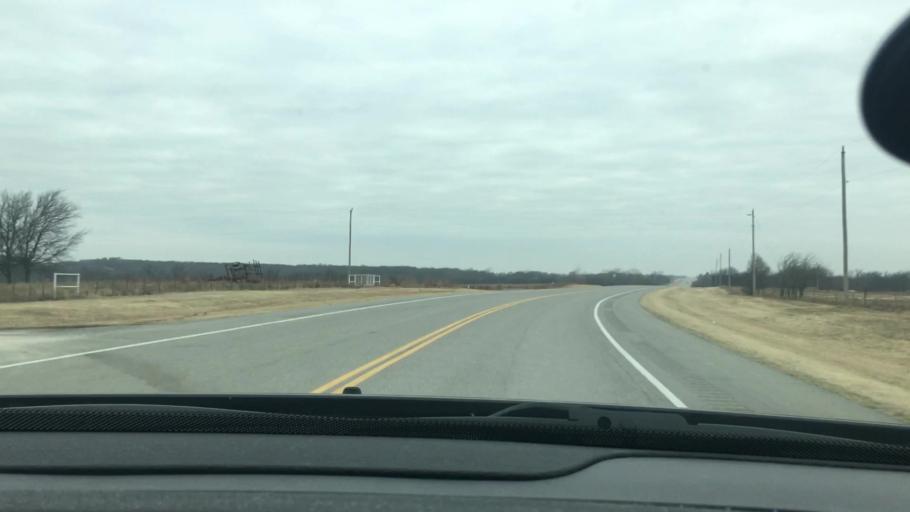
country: US
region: Oklahoma
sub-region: Murray County
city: Davis
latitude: 34.4927
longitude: -97.3712
